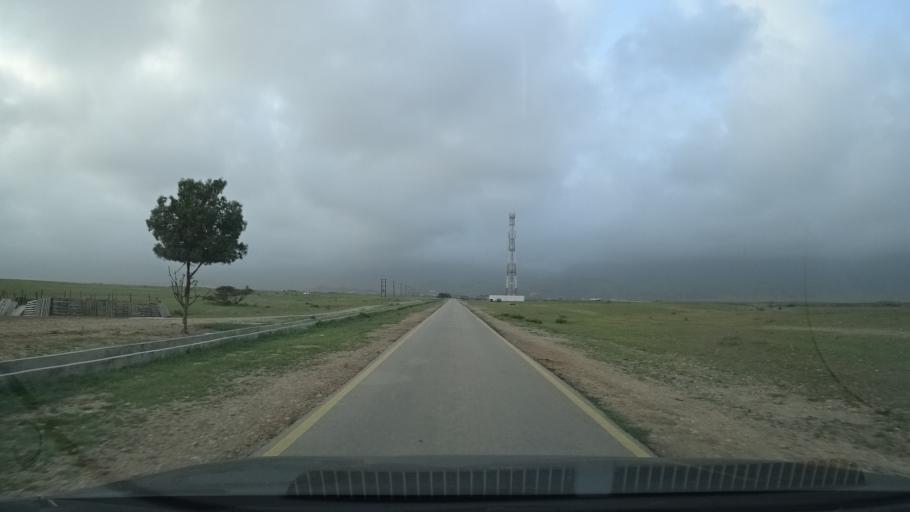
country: OM
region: Zufar
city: Salalah
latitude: 17.0843
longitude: 54.2320
